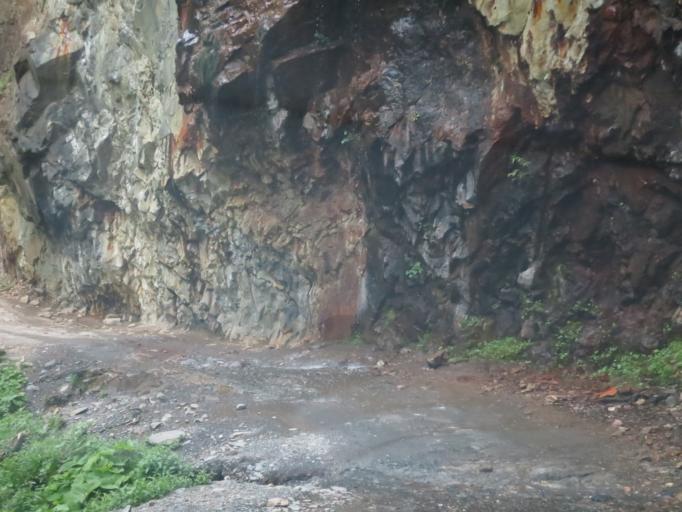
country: GE
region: Kakheti
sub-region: Telavi
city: Telavi
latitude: 42.2378
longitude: 45.4925
